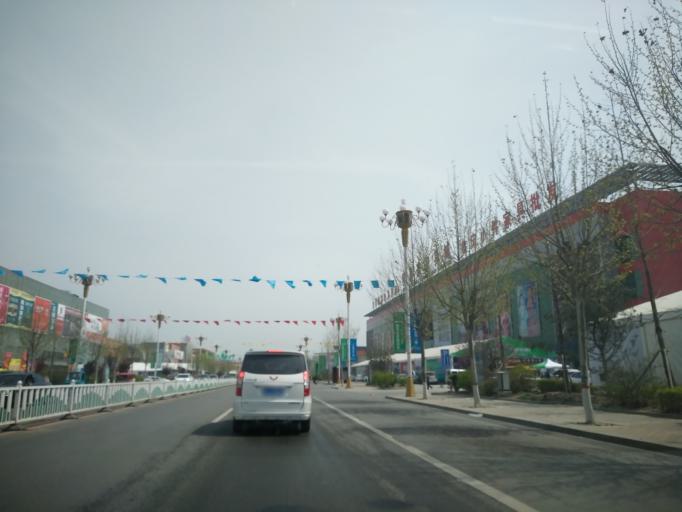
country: CN
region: Tianjin Shi
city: Xiawuqi
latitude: 39.7489
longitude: 117.0100
